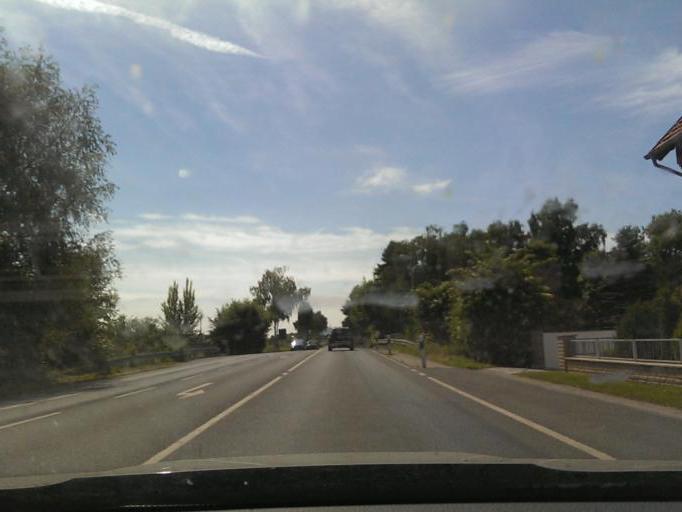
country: DE
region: Lower Saxony
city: Bruggen
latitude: 52.0116
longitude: 9.7903
